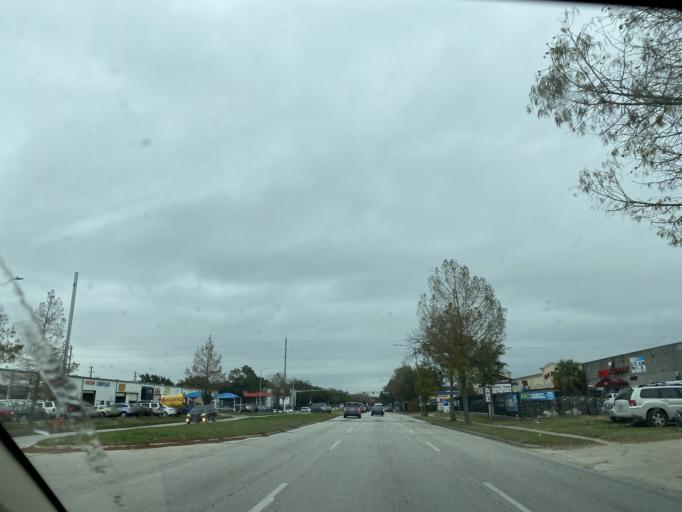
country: US
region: Texas
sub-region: Harris County
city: Piney Point Village
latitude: 29.7293
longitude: -95.5161
